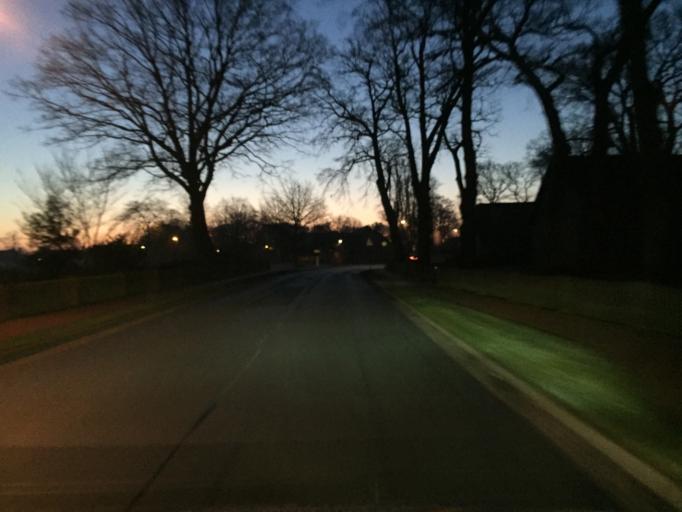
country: DE
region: Lower Saxony
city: Steyerberg
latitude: 52.5940
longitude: 8.9720
